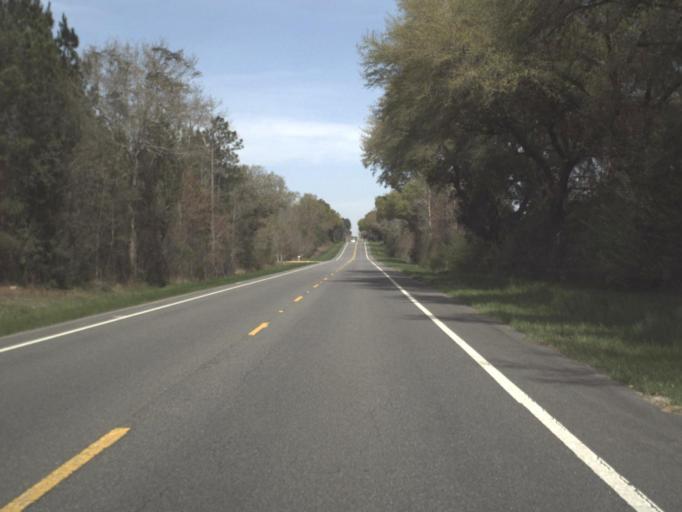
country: US
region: Florida
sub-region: Walton County
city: DeFuniak Springs
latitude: 30.8247
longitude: -85.9567
